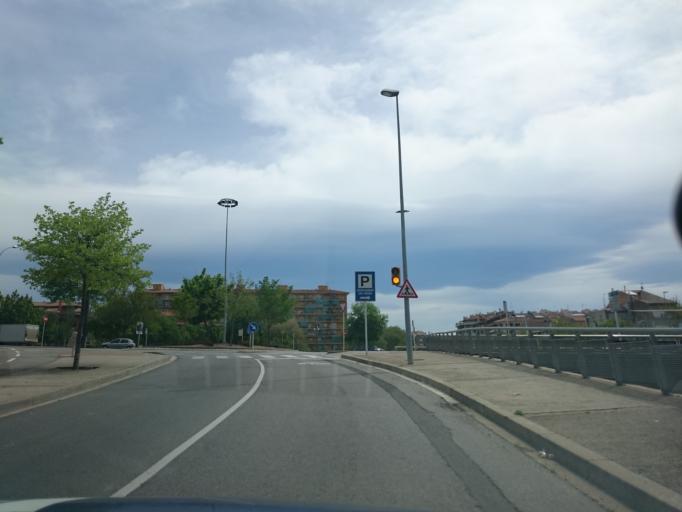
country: ES
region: Catalonia
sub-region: Provincia de Barcelona
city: Vic
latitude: 41.9247
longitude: 2.2482
